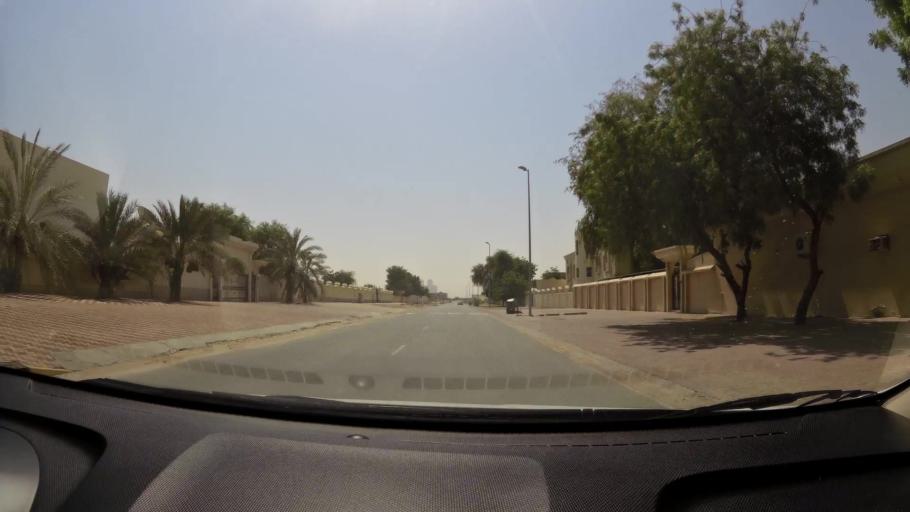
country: AE
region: Ajman
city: Ajman
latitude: 25.3940
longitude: 55.5381
